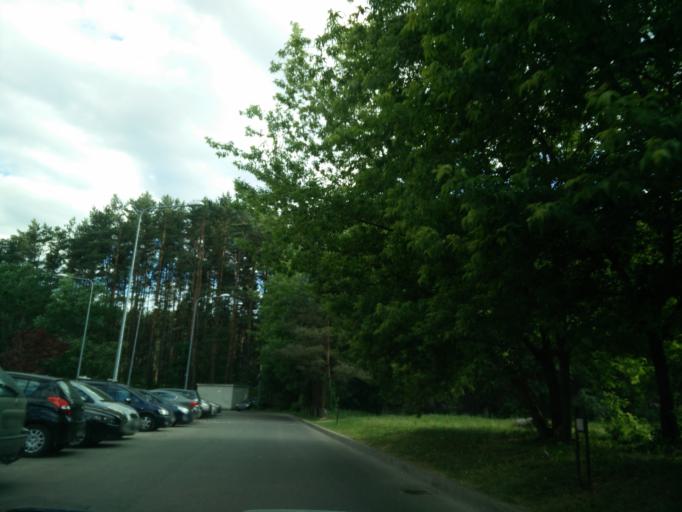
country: LT
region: Vilnius County
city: Lazdynai
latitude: 54.6673
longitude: 25.2098
